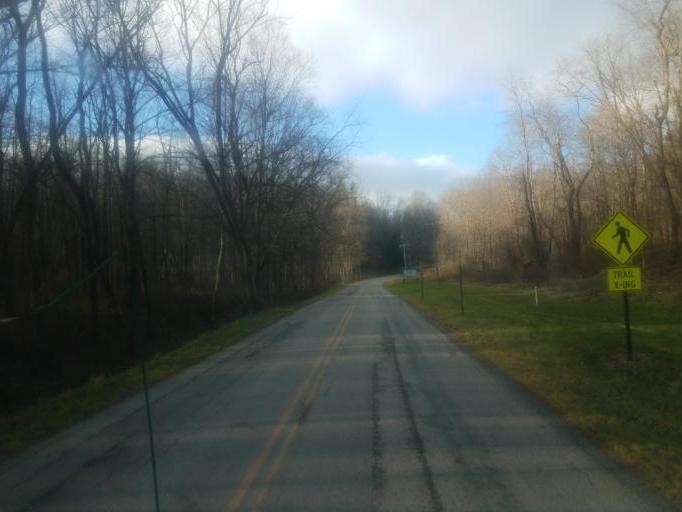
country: US
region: Ohio
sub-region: Sandusky County
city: Bellville
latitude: 40.6116
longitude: -82.3798
